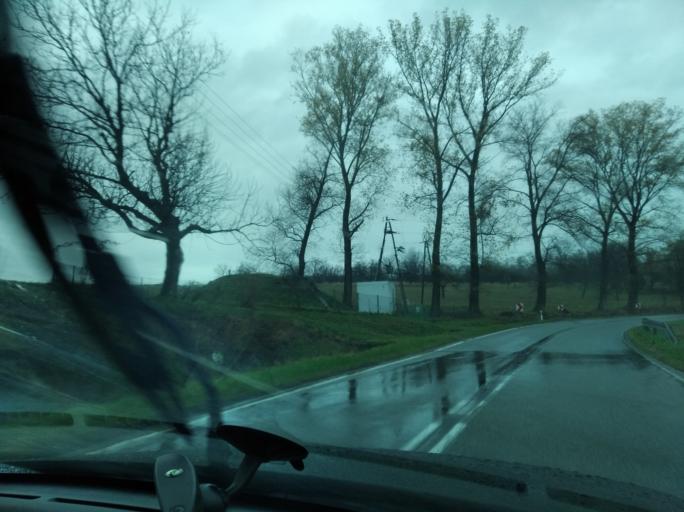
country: PL
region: Subcarpathian Voivodeship
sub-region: Powiat lancucki
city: Albigowa
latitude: 50.0087
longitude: 22.2155
